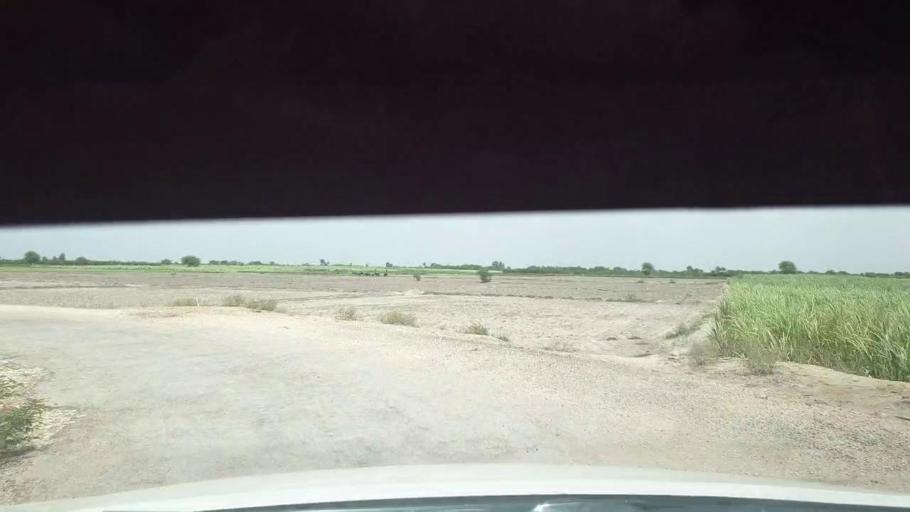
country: PK
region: Sindh
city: Kadhan
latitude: 24.5432
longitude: 69.1254
